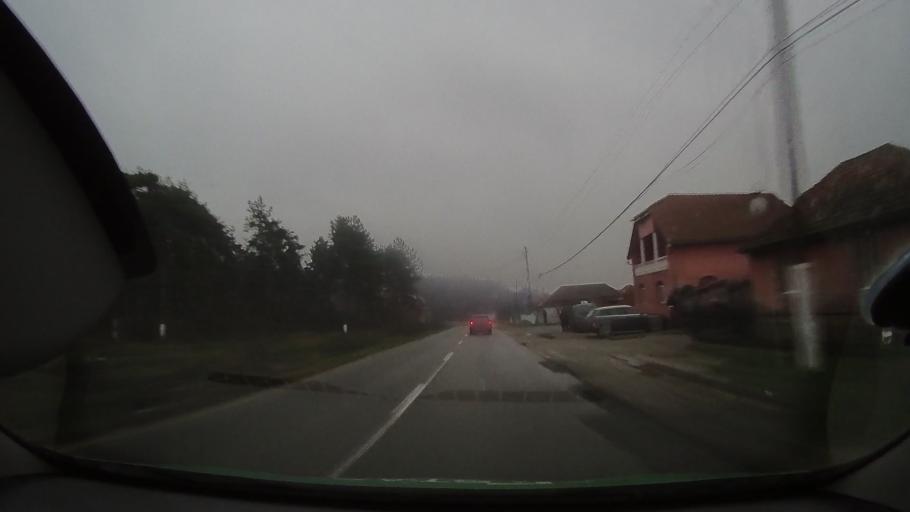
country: RO
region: Arad
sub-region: Comuna Craiova
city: Craiova
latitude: 46.5723
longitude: 21.9731
